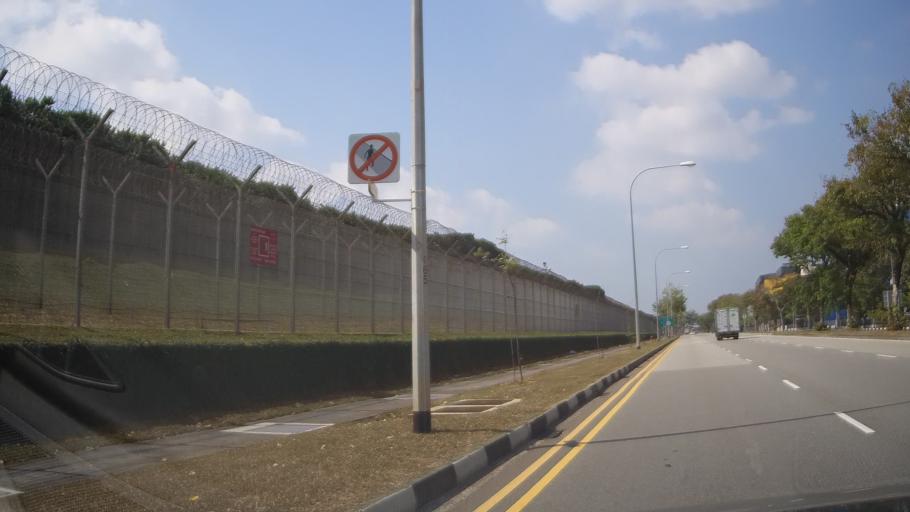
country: SG
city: Singapore
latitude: 1.3698
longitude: 103.9107
